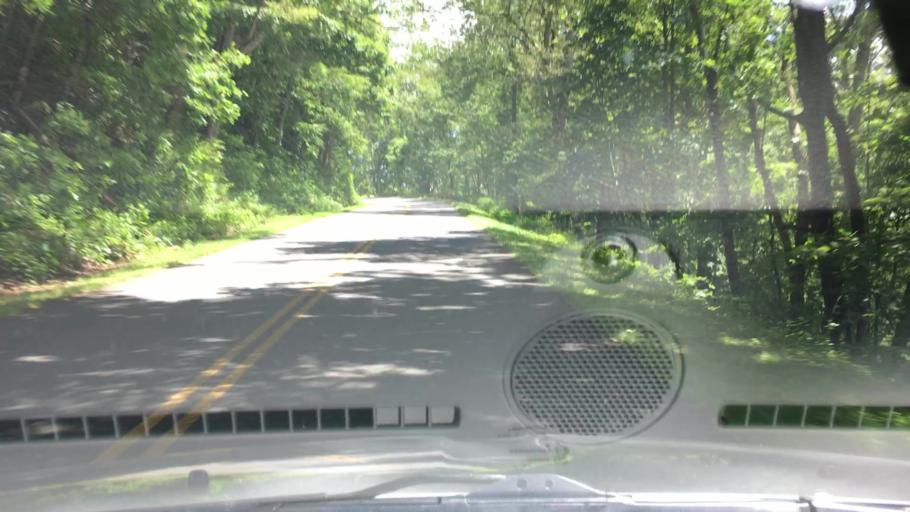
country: US
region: North Carolina
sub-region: Buncombe County
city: Swannanoa
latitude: 35.6676
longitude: -82.4450
